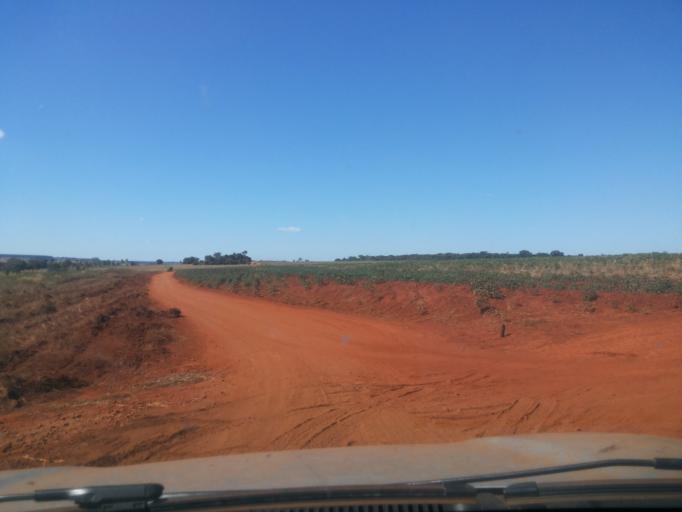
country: BR
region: Minas Gerais
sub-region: Centralina
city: Centralina
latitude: -18.7397
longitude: -49.1977
